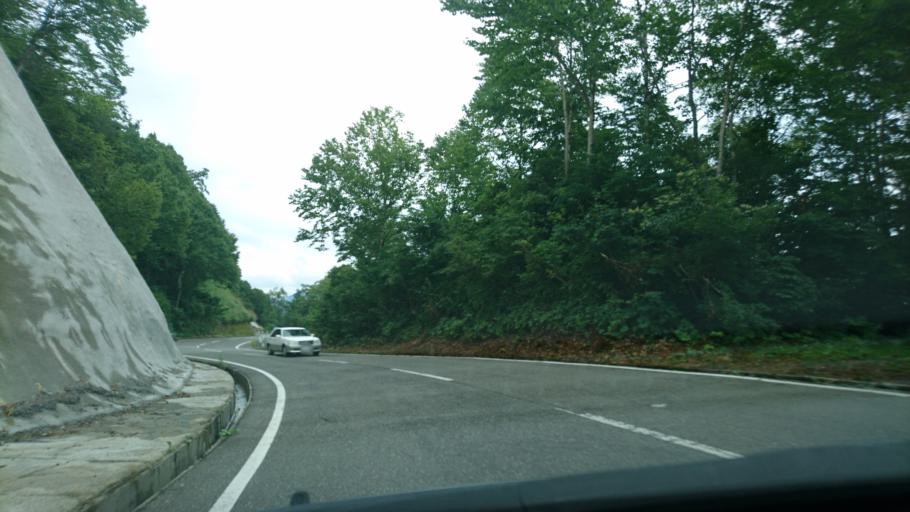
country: JP
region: Akita
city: Yuzawa
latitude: 38.9814
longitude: 140.7219
